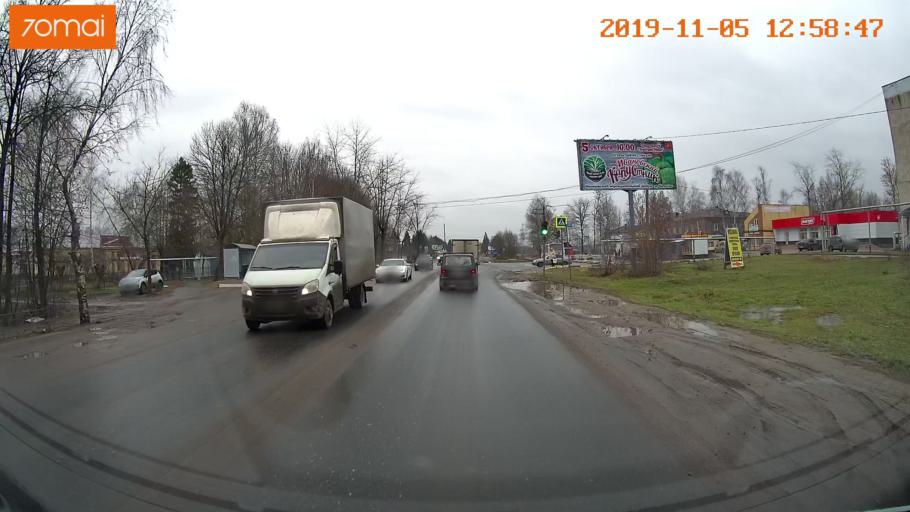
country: RU
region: Ivanovo
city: Kokhma
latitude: 56.9206
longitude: 41.1218
